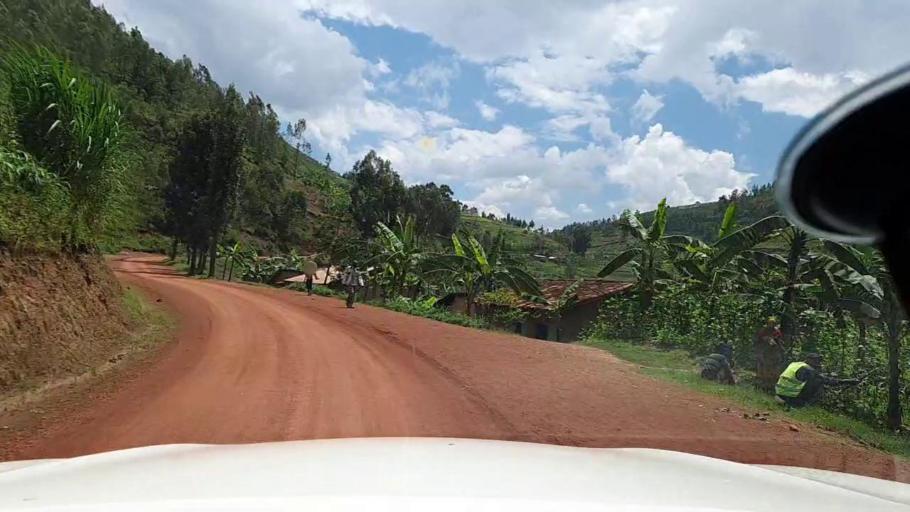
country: RW
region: Northern Province
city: Byumba
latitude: -1.7484
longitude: 29.8498
